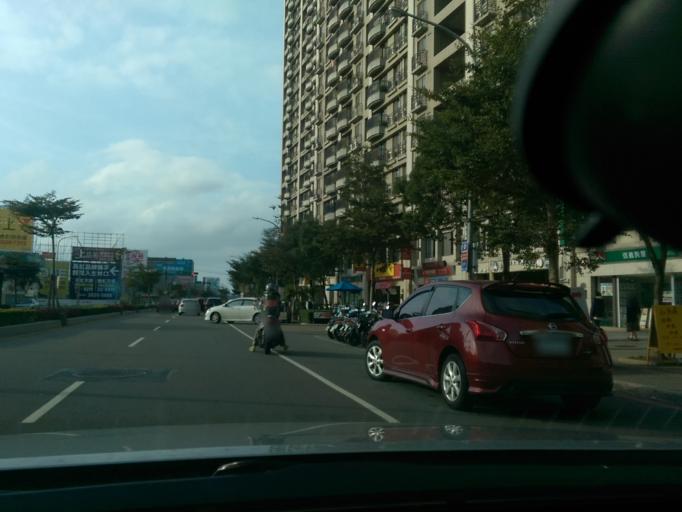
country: TW
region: Taiwan
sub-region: Taoyuan
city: Taoyuan
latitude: 25.0835
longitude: 121.3786
